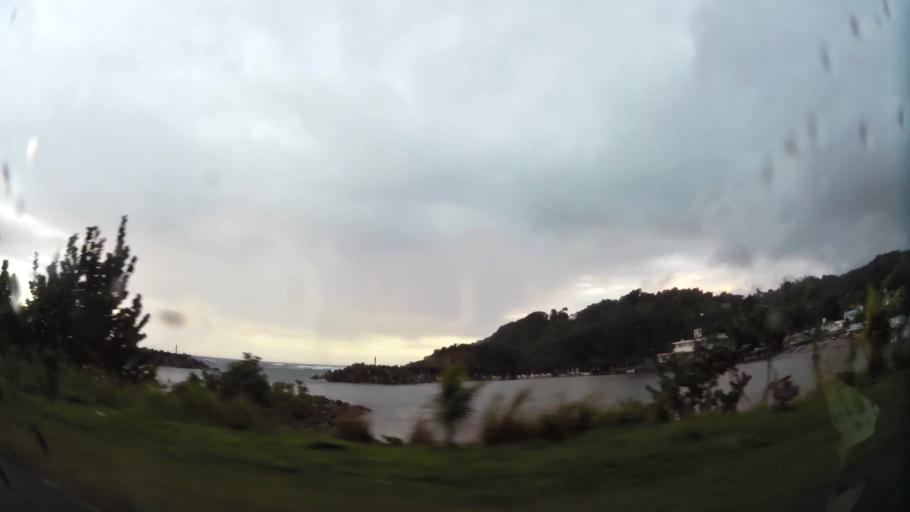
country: DM
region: Saint Andrew
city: Marigot
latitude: 15.5422
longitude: -61.2880
